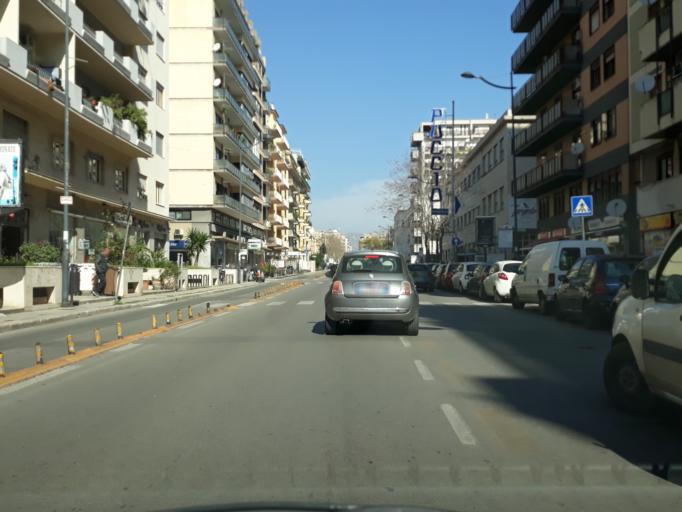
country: IT
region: Sicily
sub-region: Palermo
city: Palermo
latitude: 38.1360
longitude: 13.3512
